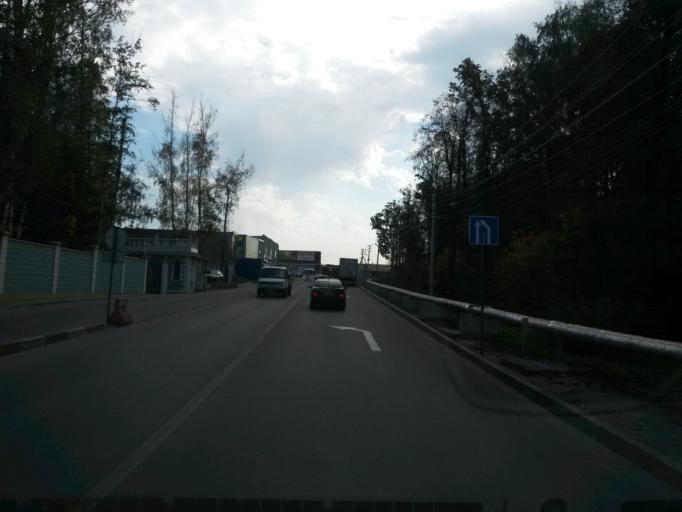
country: RU
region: Moscow
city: Tyoply Stan
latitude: 55.6123
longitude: 37.4846
